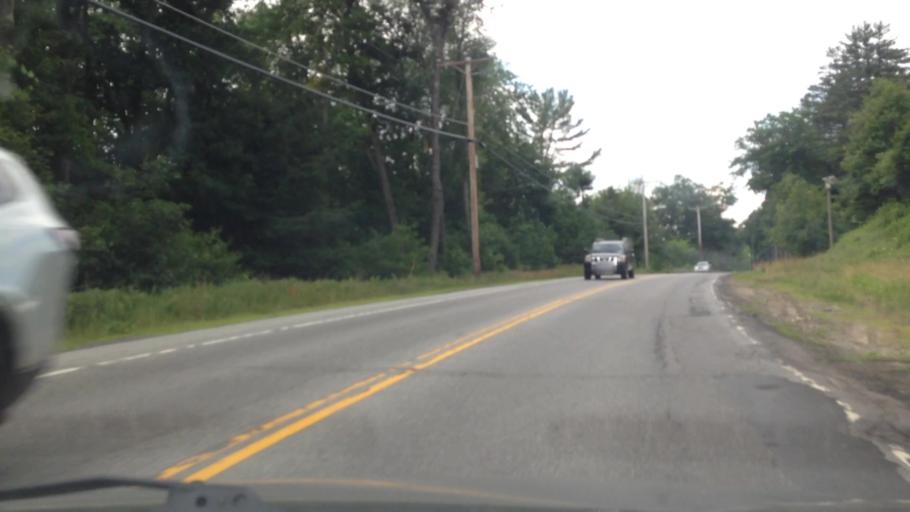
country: US
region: New Hampshire
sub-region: Cheshire County
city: Marlborough
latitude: 42.9154
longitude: -72.2276
